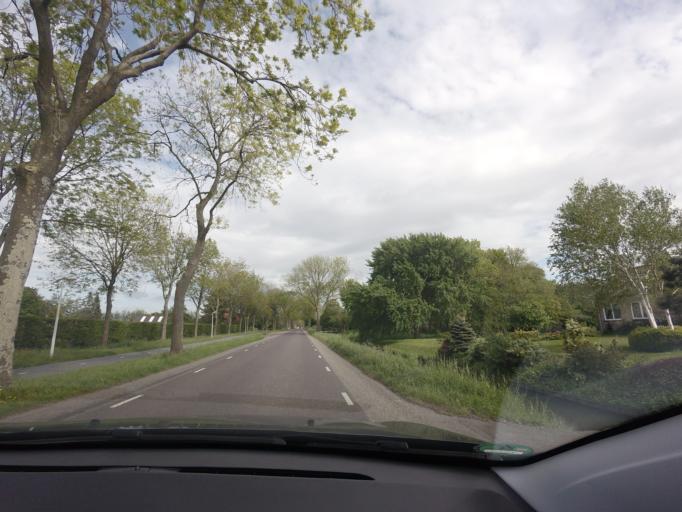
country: NL
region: North Holland
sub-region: Gemeente Beemster
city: Halfweg
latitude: 52.5211
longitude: 4.9090
